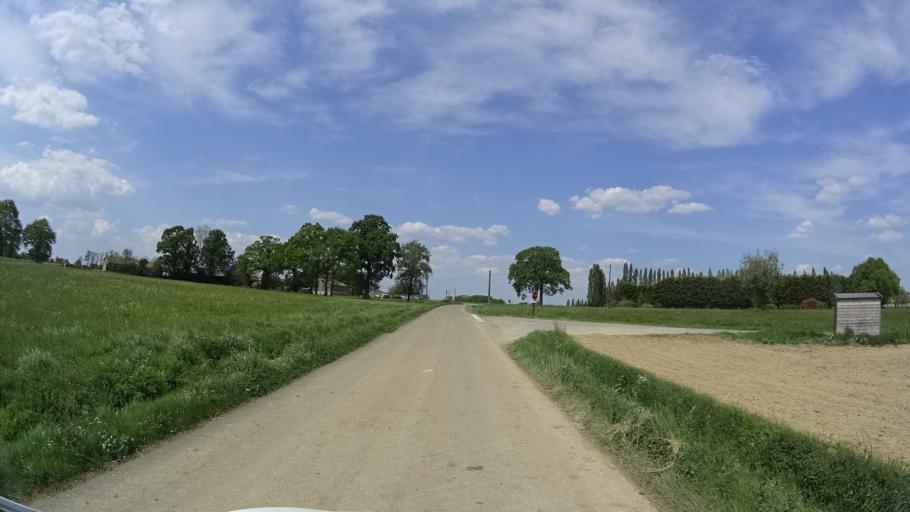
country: FR
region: Brittany
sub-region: Departement d'Ille-et-Vilaine
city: Torce
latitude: 48.0446
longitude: -1.2645
